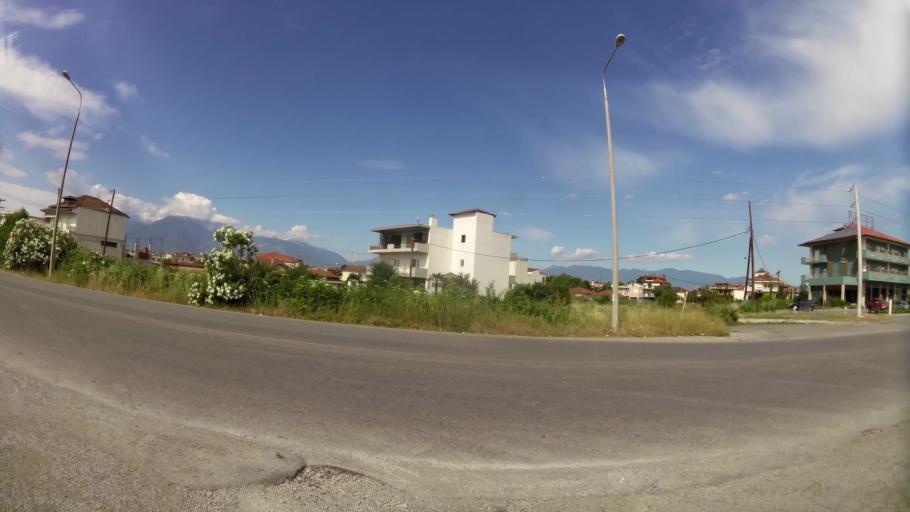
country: GR
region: Central Macedonia
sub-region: Nomos Pierias
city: Katerini
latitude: 40.2776
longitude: 22.5191
